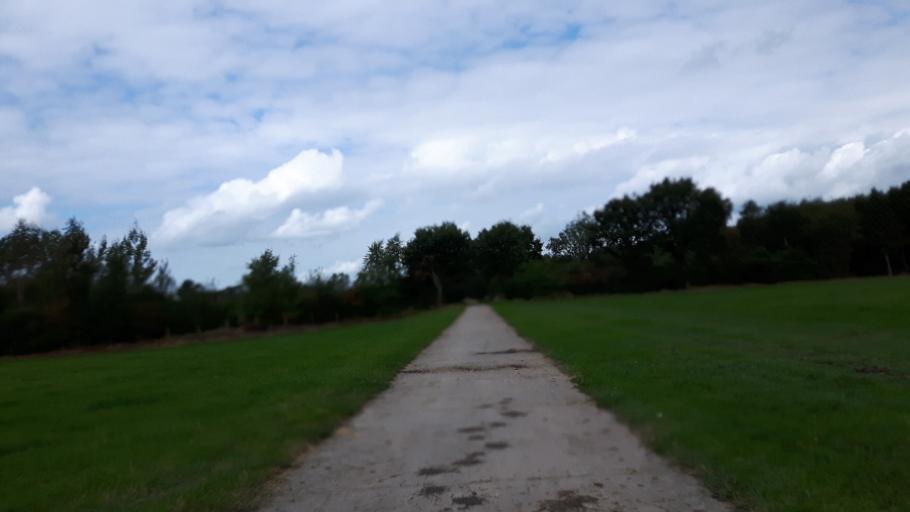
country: NL
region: Groningen
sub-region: Gemeente Leek
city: Leek
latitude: 53.0825
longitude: 6.3242
